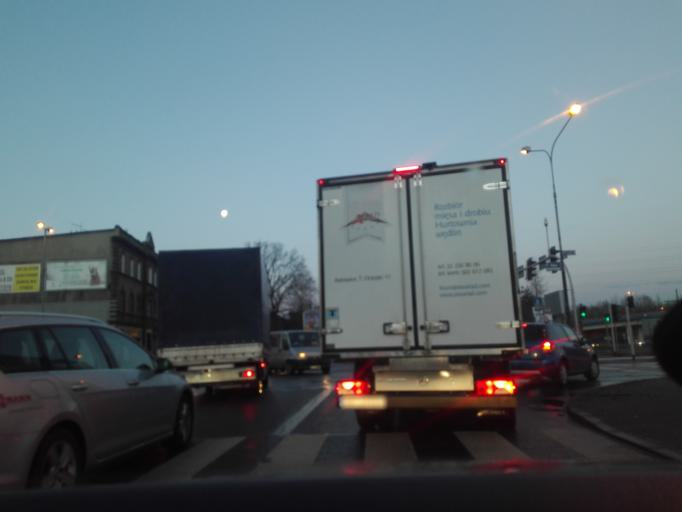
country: PL
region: Silesian Voivodeship
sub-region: Katowice
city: Katowice
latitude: 50.2673
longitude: 18.9901
